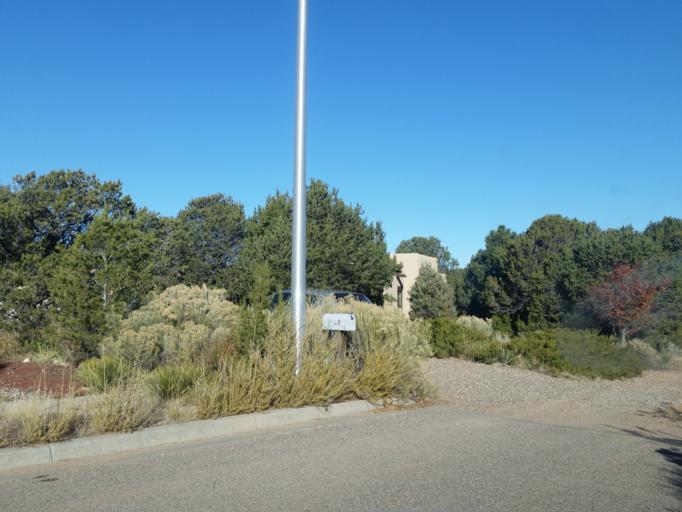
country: US
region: New Mexico
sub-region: Santa Fe County
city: Santa Fe
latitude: 35.6510
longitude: -105.9280
